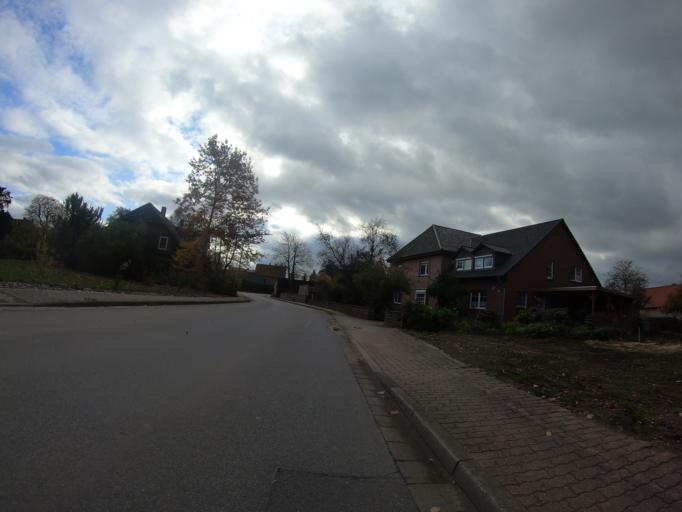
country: DE
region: Lower Saxony
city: Ribbesbuttel
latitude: 52.4246
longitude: 10.4837
